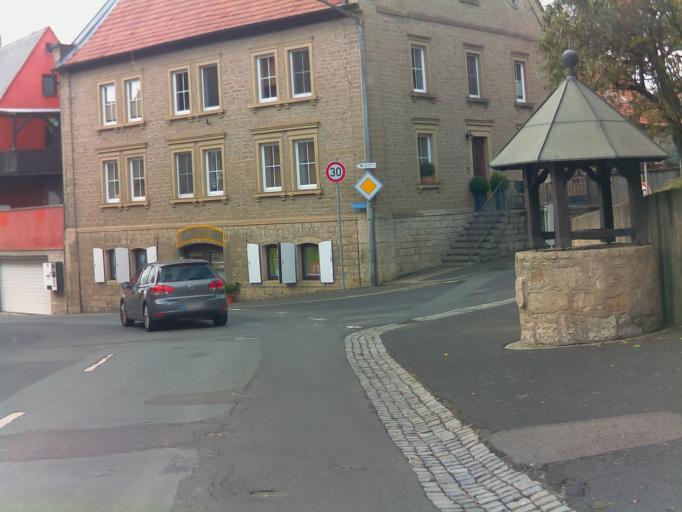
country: DE
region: Bavaria
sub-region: Regierungsbezirk Unterfranken
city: Geroldshausen
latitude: 49.6939
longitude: 9.9326
